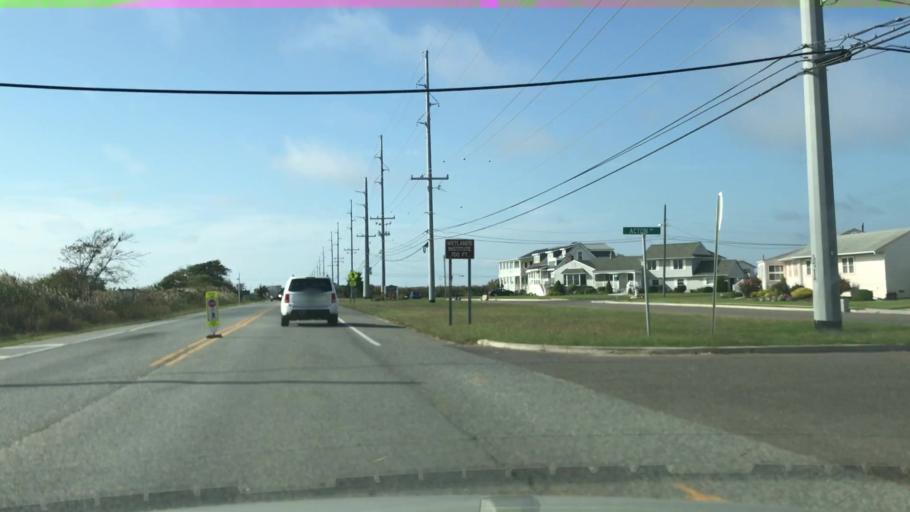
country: US
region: New Jersey
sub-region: Cape May County
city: Cape May Court House
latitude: 39.0600
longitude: -74.7704
